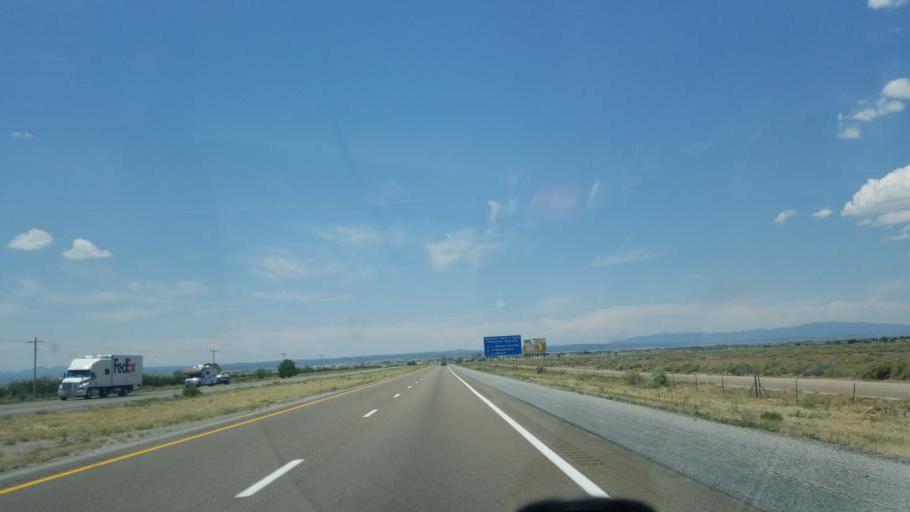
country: US
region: New Mexico
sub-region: Torrance County
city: Moriarty
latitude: 35.0049
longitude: -105.9792
